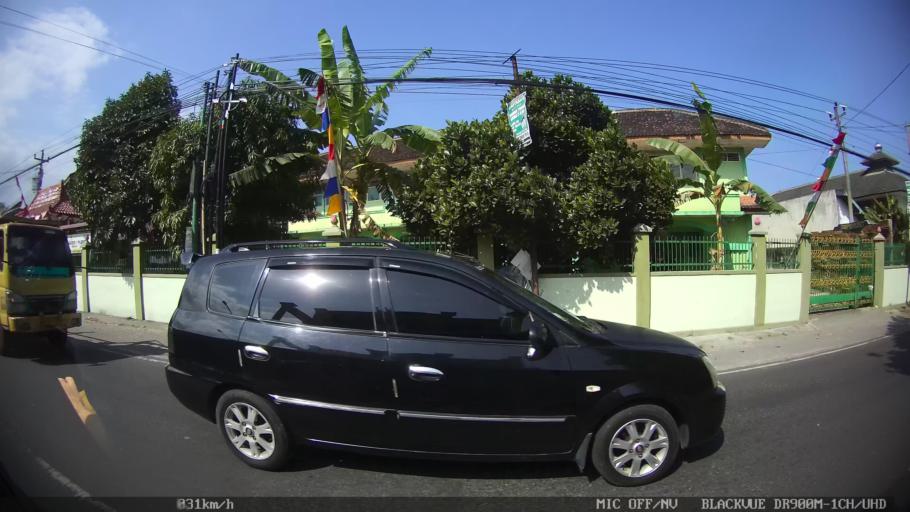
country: ID
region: Daerah Istimewa Yogyakarta
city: Sewon
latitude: -7.8691
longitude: 110.3908
